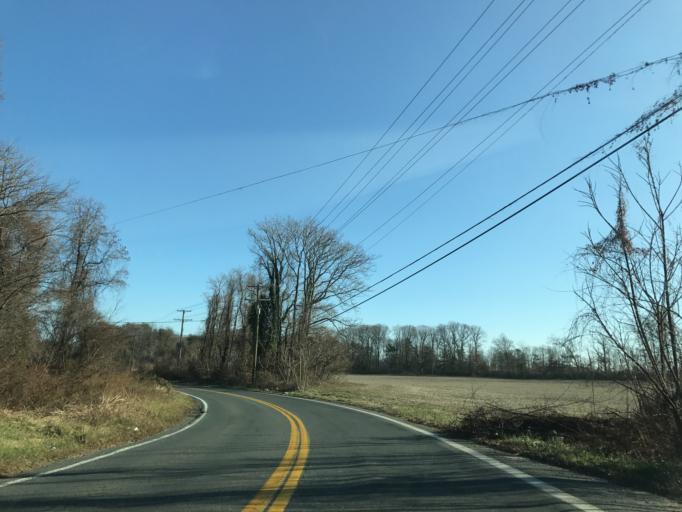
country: US
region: Maryland
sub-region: Baltimore County
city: Bowleys Quarters
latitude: 39.3637
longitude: -76.3995
